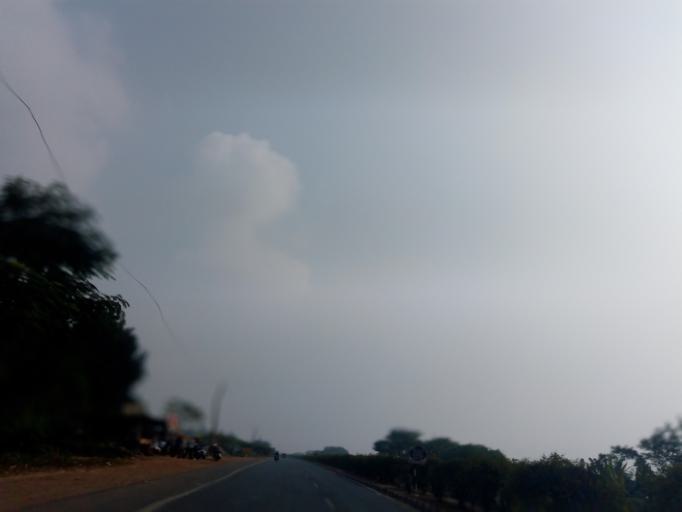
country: IN
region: Andhra Pradesh
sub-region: West Godavari
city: Tadepallegudem
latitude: 16.8131
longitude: 81.3751
